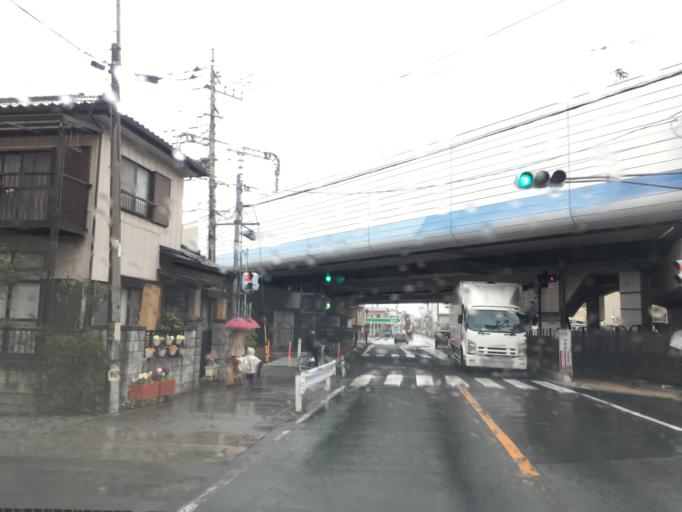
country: JP
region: Saitama
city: Koshigaya
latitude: 35.8893
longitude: 139.7854
